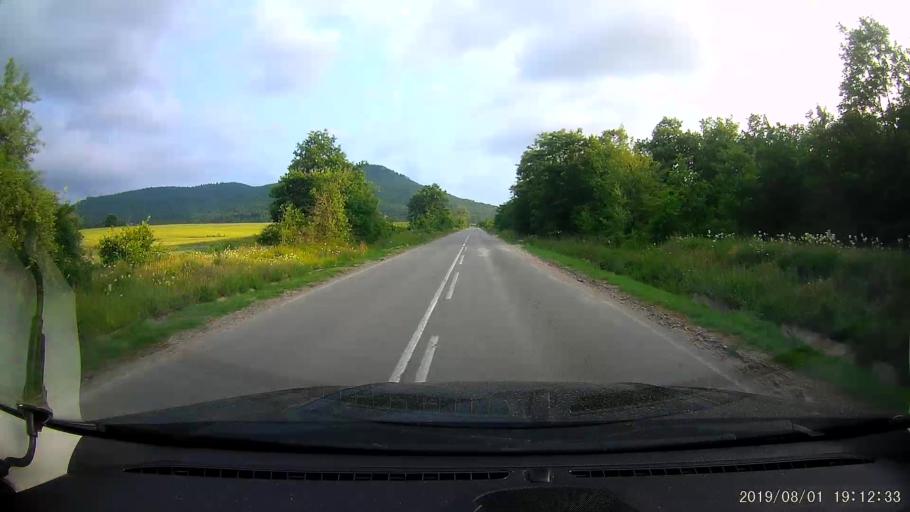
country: BG
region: Shumen
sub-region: Obshtina Smyadovo
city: Smyadovo
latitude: 42.9633
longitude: 26.9498
